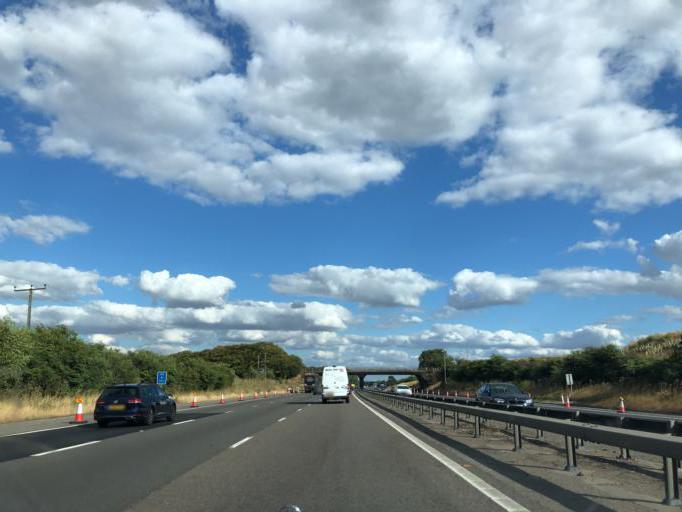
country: GB
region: England
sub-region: Milton Keynes
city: Moulsoe
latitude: 52.0478
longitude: -0.6674
